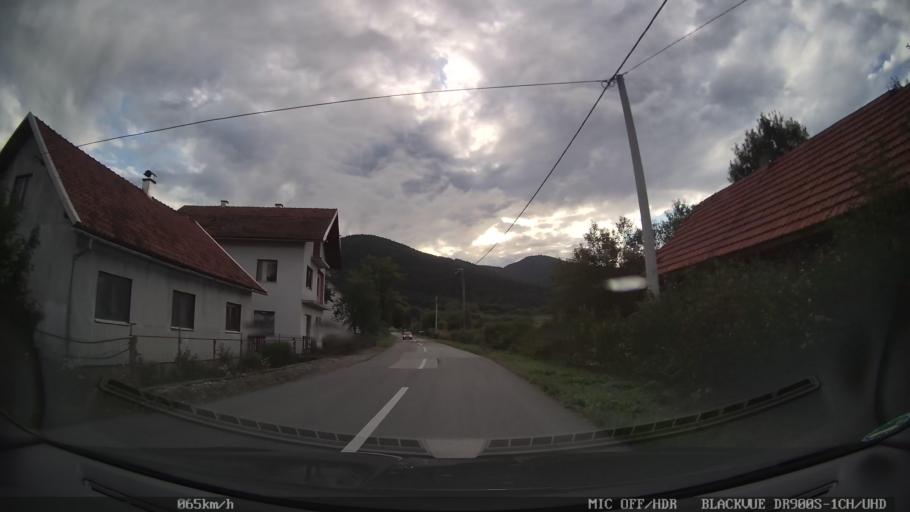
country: HR
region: Karlovacka
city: Plaski
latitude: 44.9946
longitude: 15.4318
